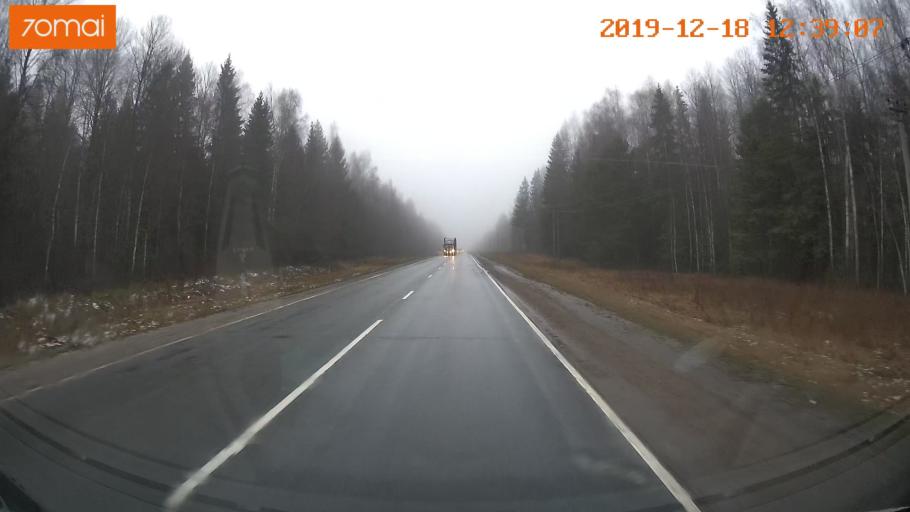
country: RU
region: Moskovskaya
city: Vysokovsk
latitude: 56.1607
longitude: 36.6093
